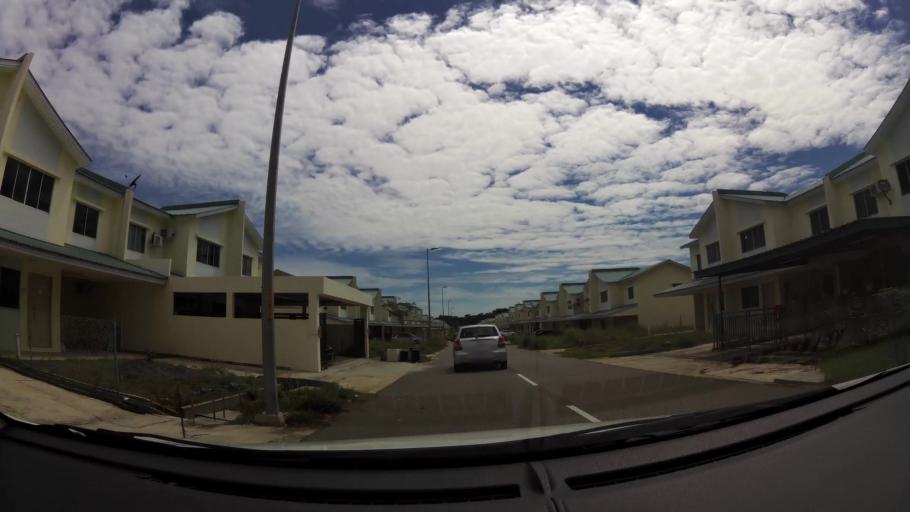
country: BN
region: Brunei and Muara
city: Bandar Seri Begawan
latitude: 4.9737
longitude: 115.0093
